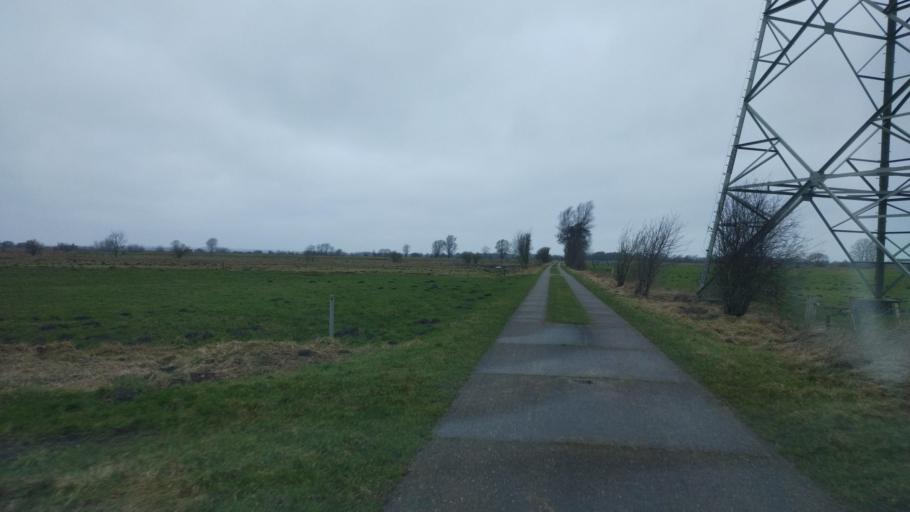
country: DE
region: Schleswig-Holstein
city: Gross Rheide
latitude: 54.4570
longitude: 9.4235
